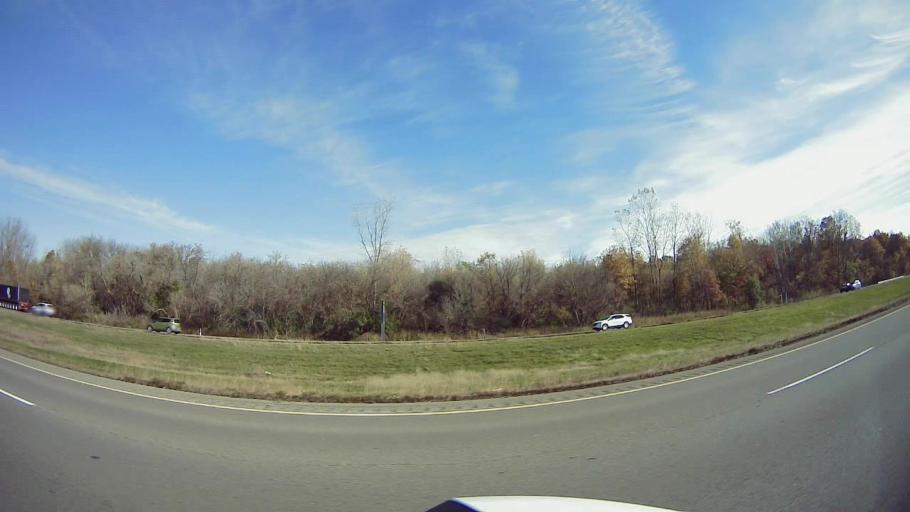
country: US
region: Michigan
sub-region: Wayne County
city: Romulus
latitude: 42.2322
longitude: -83.4348
